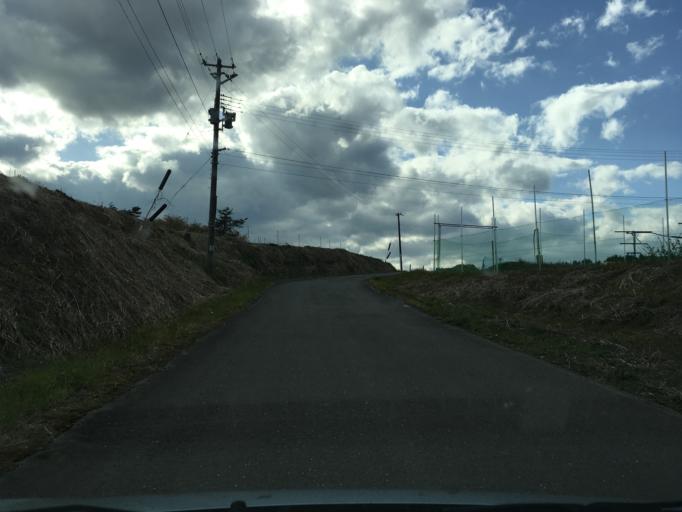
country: JP
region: Iwate
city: Ichinoseki
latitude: 38.7937
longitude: 141.4170
